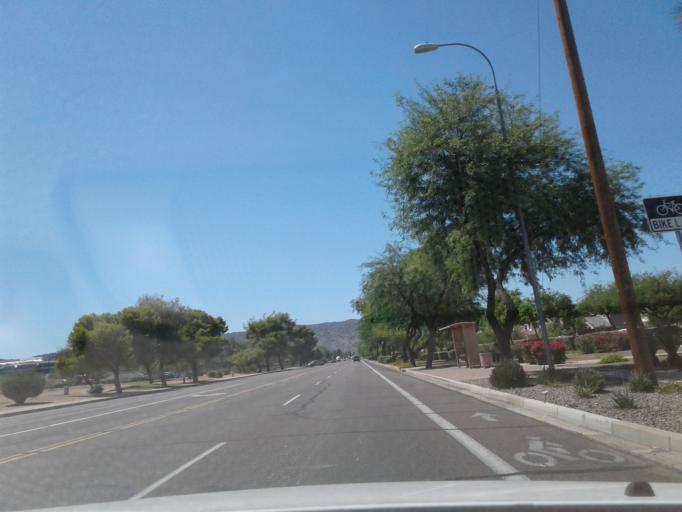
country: US
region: Arizona
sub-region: Maricopa County
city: Phoenix
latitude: 33.3996
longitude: -112.0300
